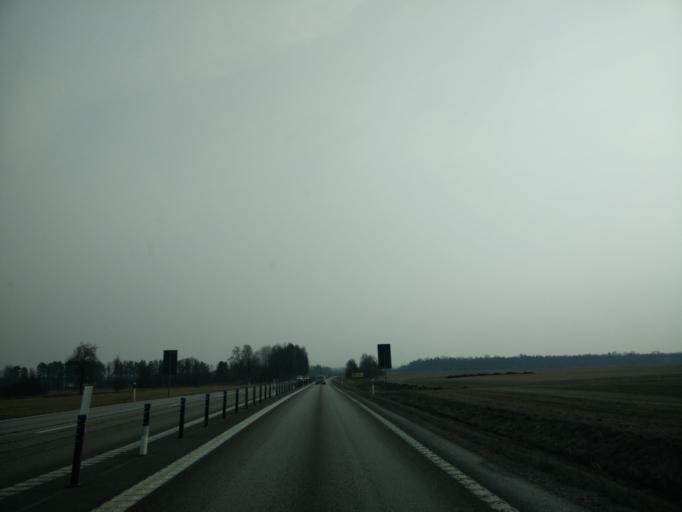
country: SE
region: Vaermland
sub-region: Karlstads Kommun
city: Karlstad
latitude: 59.4368
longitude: 13.4143
